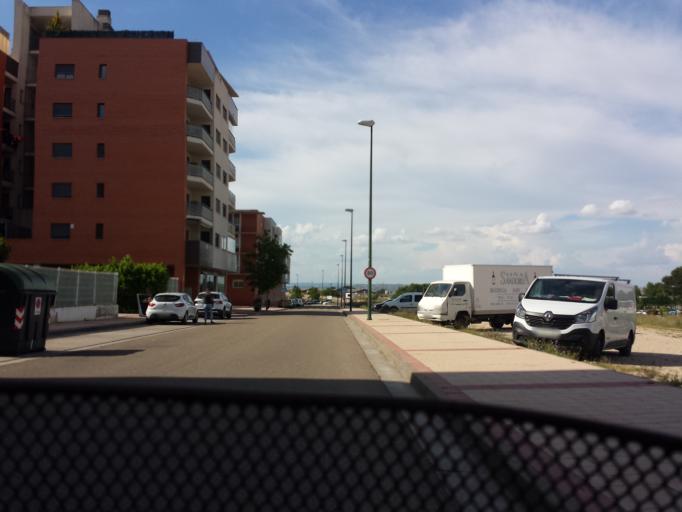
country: ES
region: Aragon
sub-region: Provincia de Zaragoza
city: Montecanal
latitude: 41.6366
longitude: -0.9445
